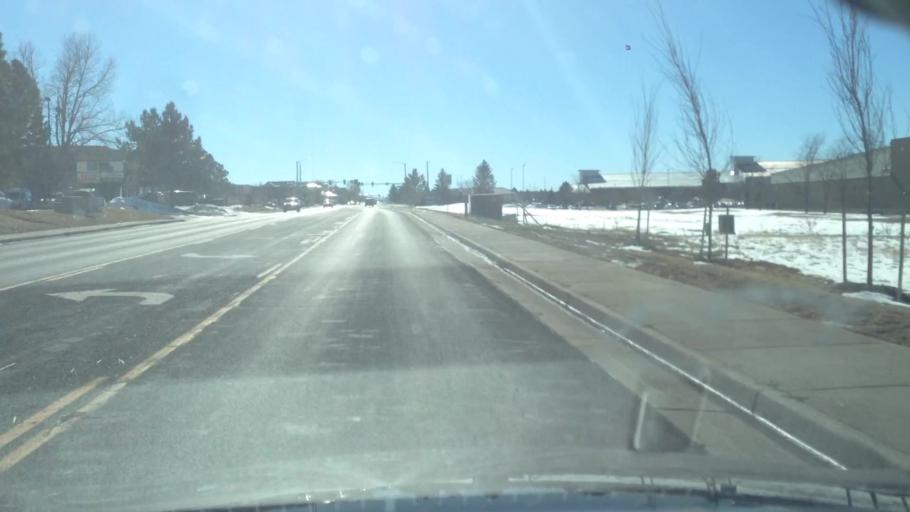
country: US
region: Colorado
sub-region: Douglas County
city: Parker
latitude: 39.5290
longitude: -104.7716
